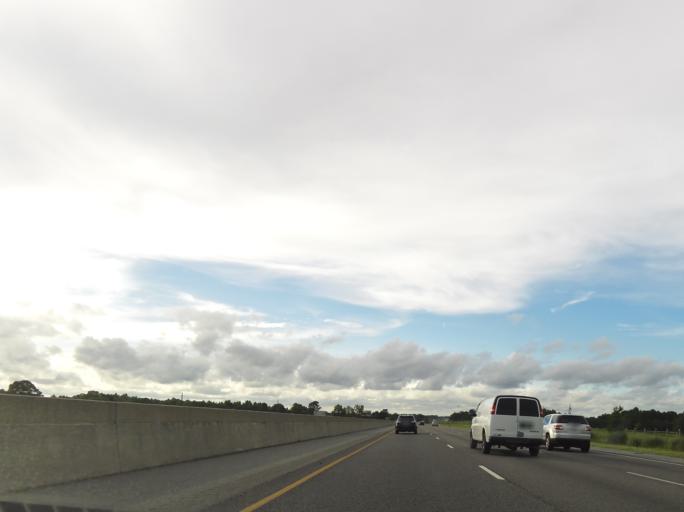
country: US
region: Georgia
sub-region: Tift County
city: Tifton
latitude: 31.5868
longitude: -83.5558
